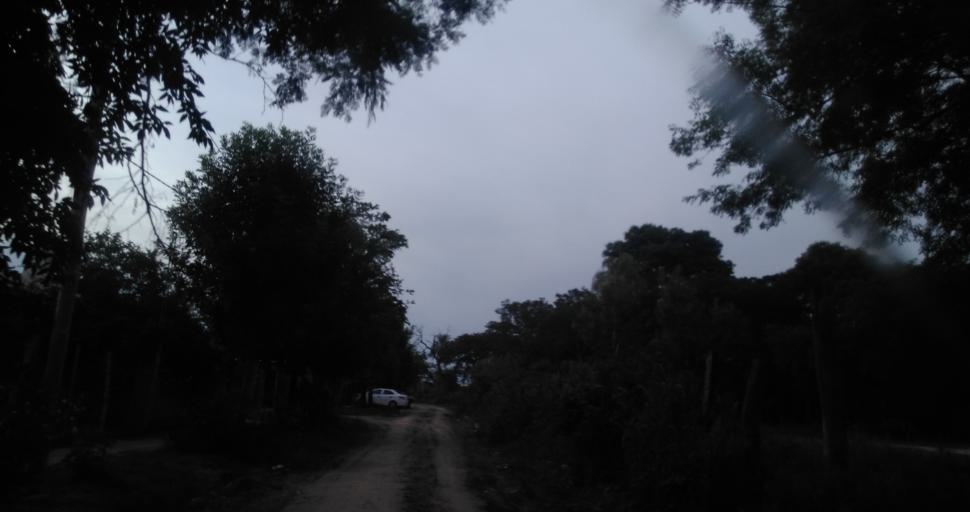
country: AR
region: Chaco
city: Fontana
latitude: -27.4099
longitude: -59.0259
